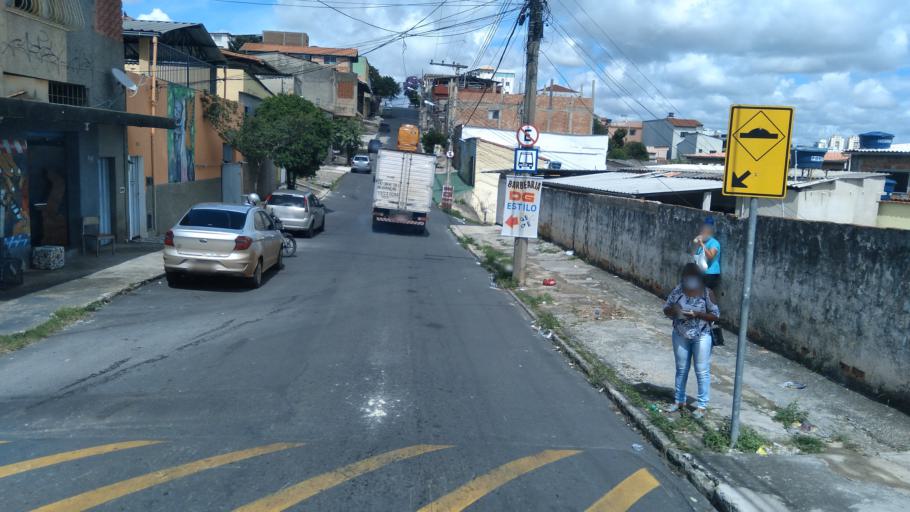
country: BR
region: Minas Gerais
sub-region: Belo Horizonte
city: Belo Horizonte
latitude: -19.8854
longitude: -43.8977
